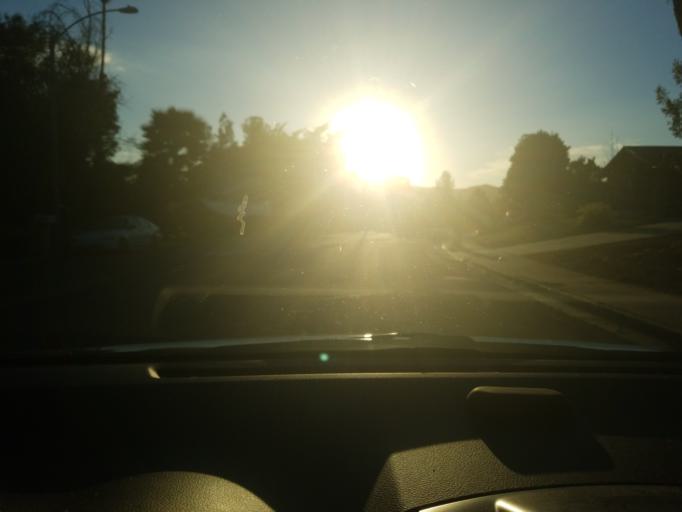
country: US
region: California
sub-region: Riverside County
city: Temecula
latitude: 33.5046
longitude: -117.1324
